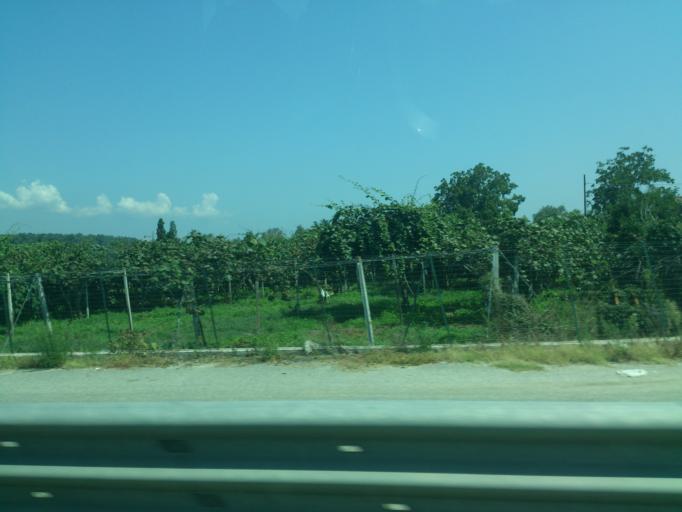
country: IT
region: Calabria
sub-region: Provincia di Reggio Calabria
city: Rosarno
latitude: 38.4690
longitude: 16.0066
